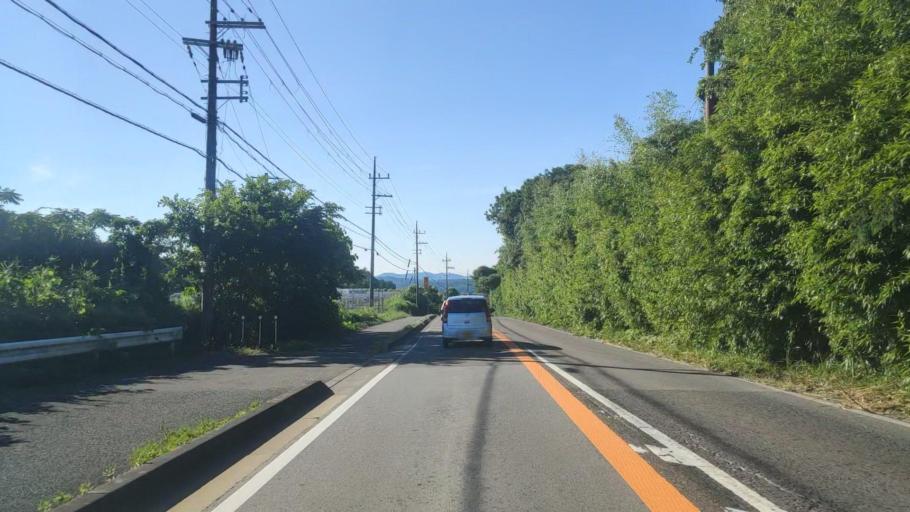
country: JP
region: Shiga Prefecture
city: Hino
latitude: 35.0376
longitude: 136.2441
